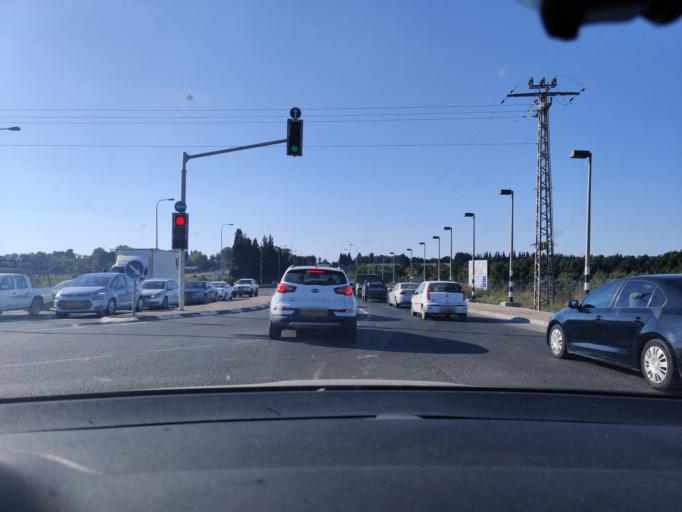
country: PS
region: West Bank
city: Nazlat `Isa
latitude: 32.4438
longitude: 35.0221
